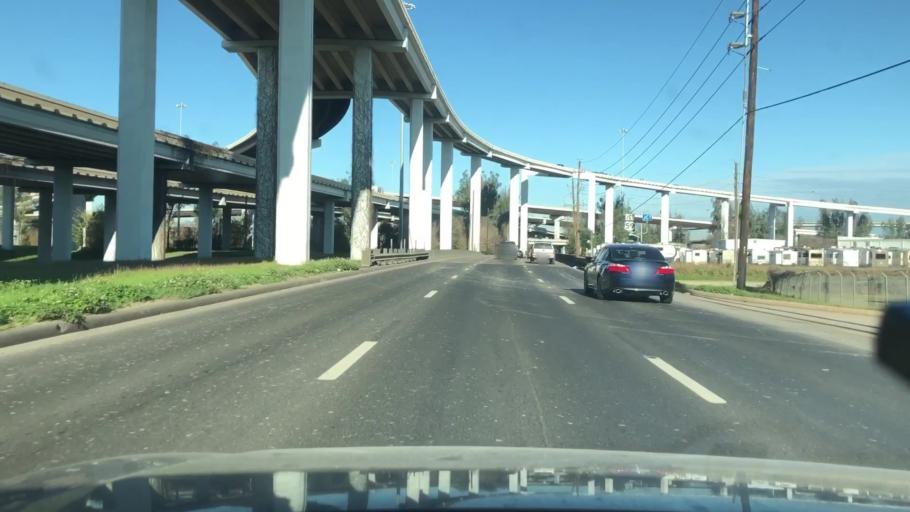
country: US
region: Texas
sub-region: Fort Bend County
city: Meadows Place
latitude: 29.6582
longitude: -95.5550
